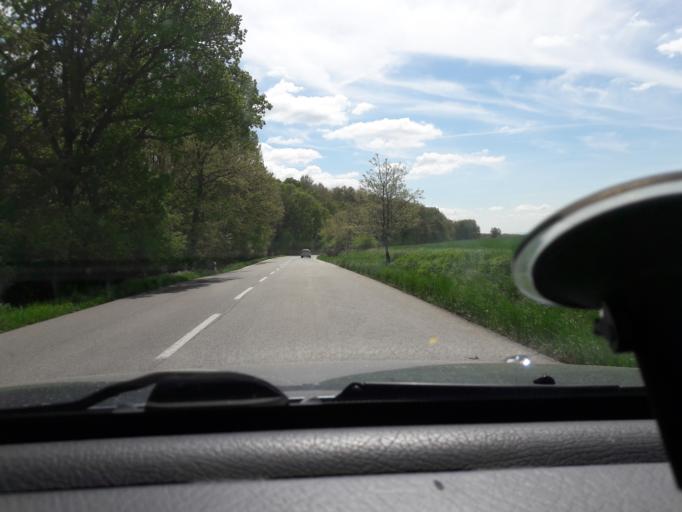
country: SK
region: Banskobystricky
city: Dudince
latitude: 48.2606
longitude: 18.7836
